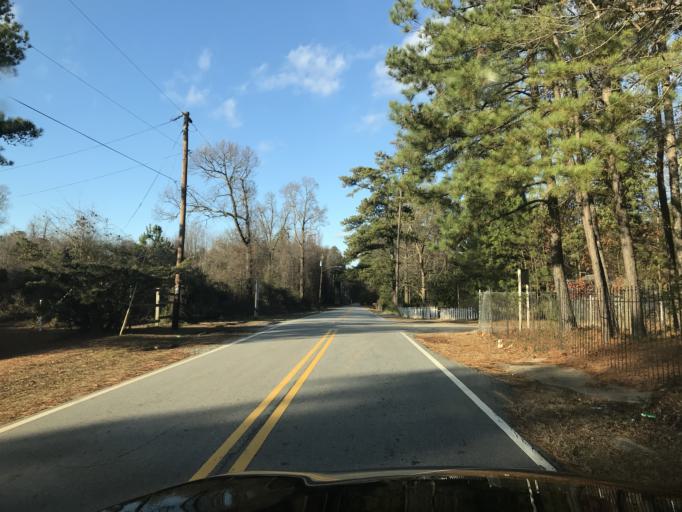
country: US
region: Georgia
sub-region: Fulton County
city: College Park
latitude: 33.6269
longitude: -84.4875
